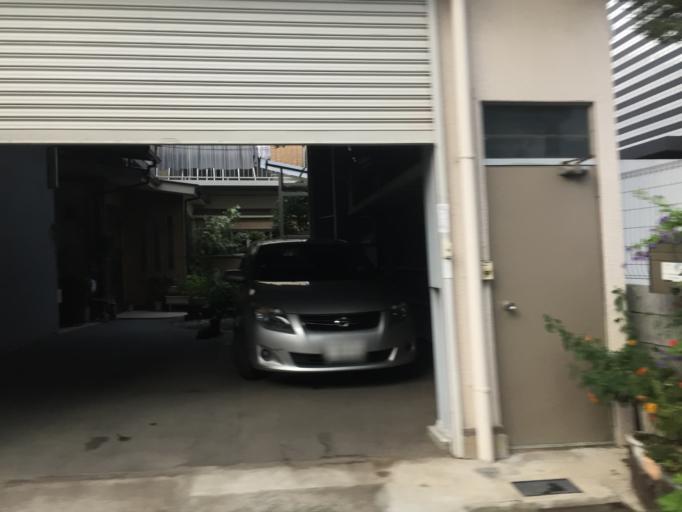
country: JP
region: Kanagawa
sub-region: Kawasaki-shi
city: Kawasaki
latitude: 35.5616
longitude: 139.6926
